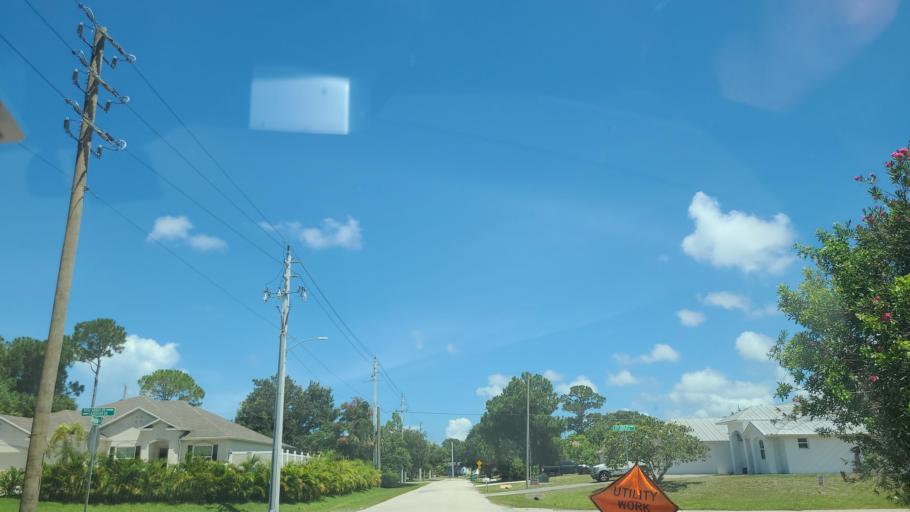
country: US
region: Florida
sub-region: Indian River County
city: Sebastian
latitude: 27.7865
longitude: -80.4869
